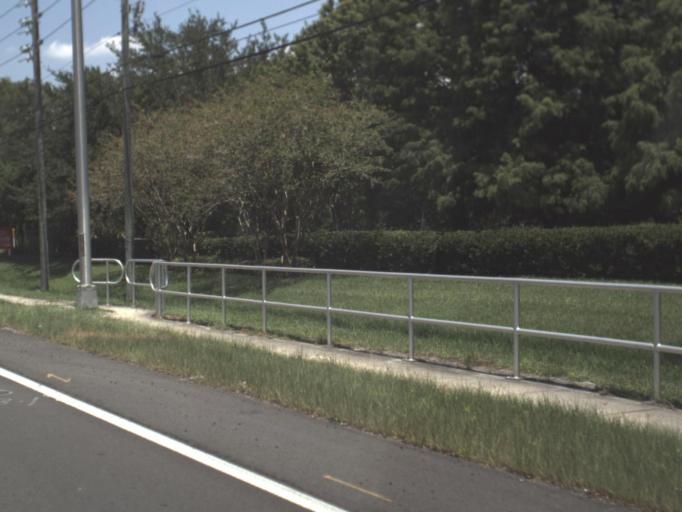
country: US
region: Florida
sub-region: Pinellas County
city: Saint George
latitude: 28.0629
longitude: -82.7387
